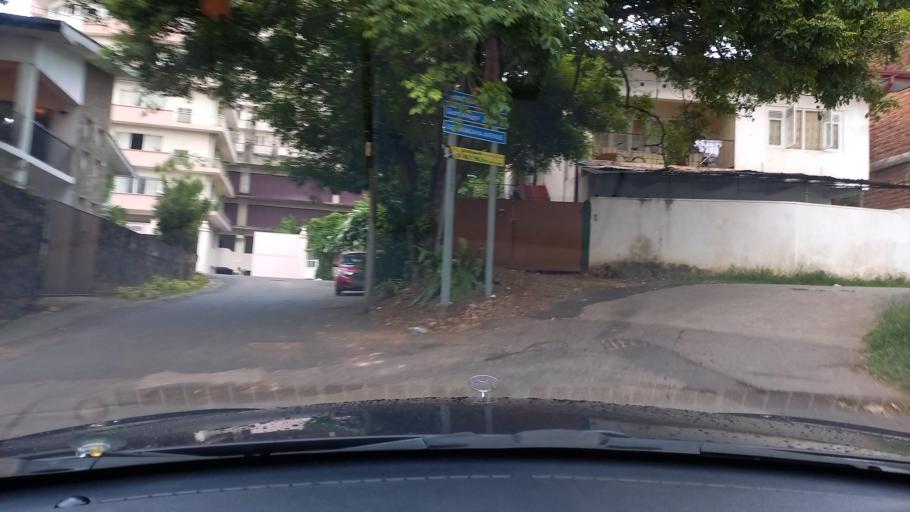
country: LK
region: Western
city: Pita Kotte
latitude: 6.8788
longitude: 79.8678
